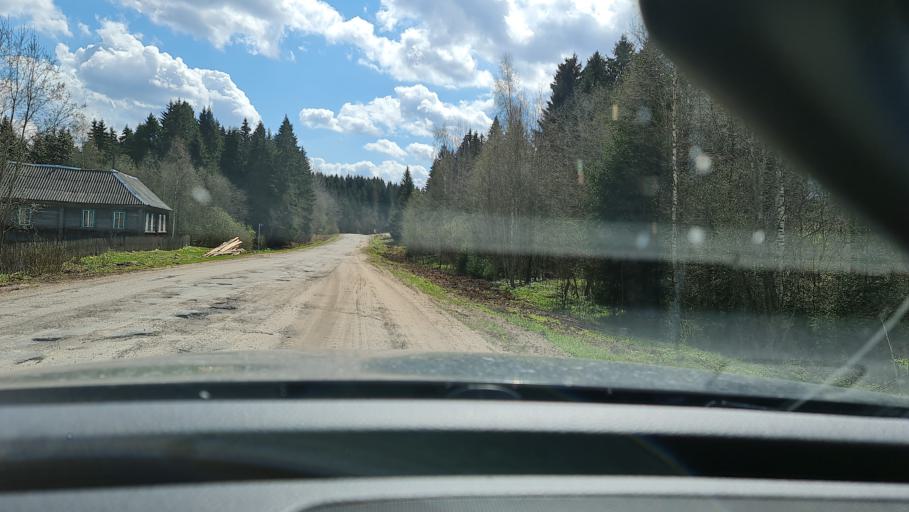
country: RU
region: Tverskaya
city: Toropets
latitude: 56.6409
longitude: 31.4225
